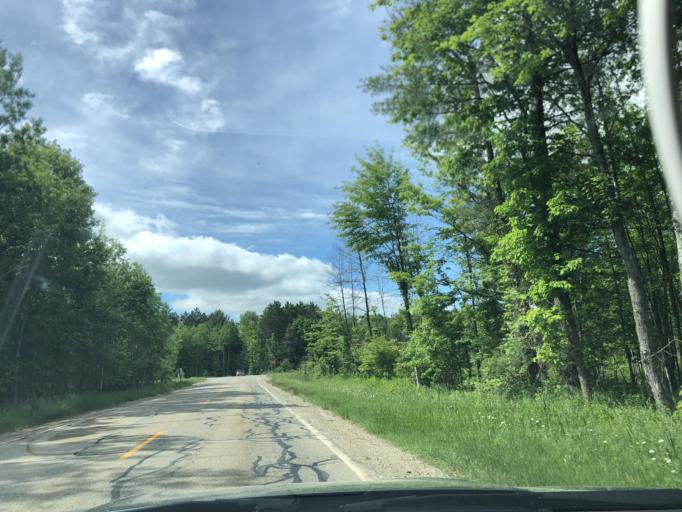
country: US
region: Michigan
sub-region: Roscommon County
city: Houghton Lake
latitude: 44.3370
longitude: -84.8544
